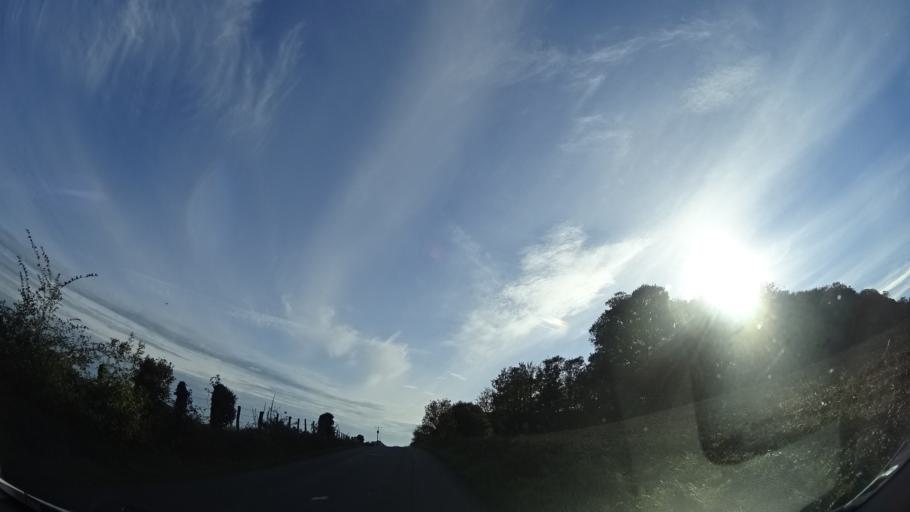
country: FR
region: Brittany
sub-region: Departement d'Ille-et-Vilaine
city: Geveze
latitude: 48.2130
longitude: -1.7914
